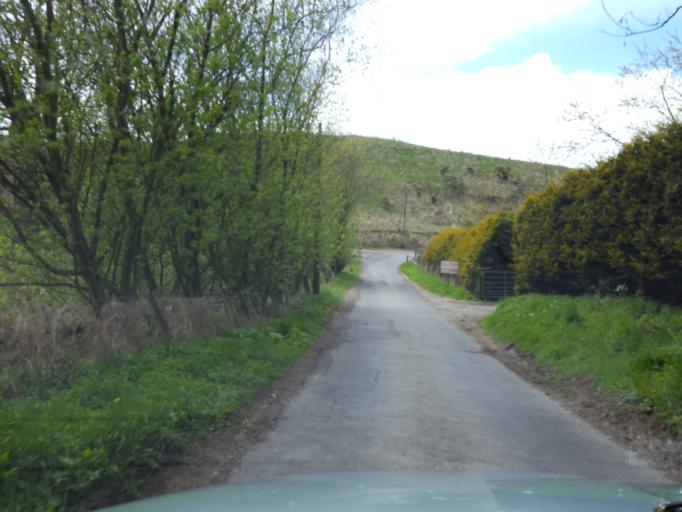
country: GB
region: Scotland
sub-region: Perth and Kinross
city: Scone
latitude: 56.4367
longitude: -3.3220
